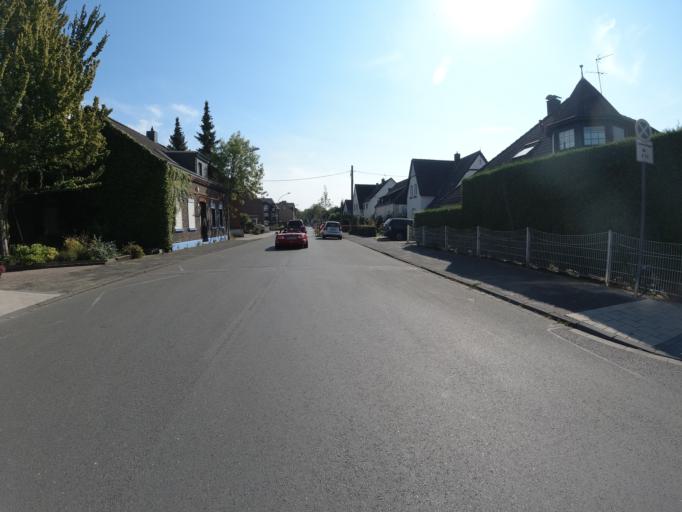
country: DE
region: North Rhine-Westphalia
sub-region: Regierungsbezirk Dusseldorf
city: Moers
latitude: 51.4612
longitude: 6.6924
